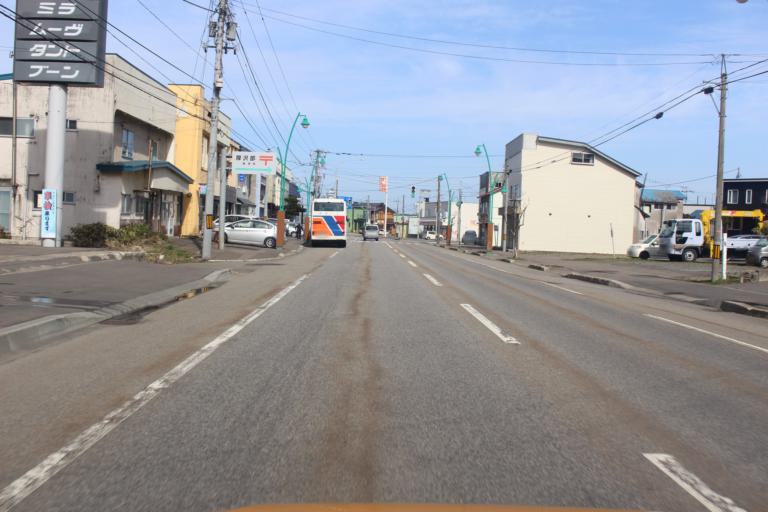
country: JP
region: Hokkaido
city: Kamiiso
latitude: 41.9161
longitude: 140.2248
